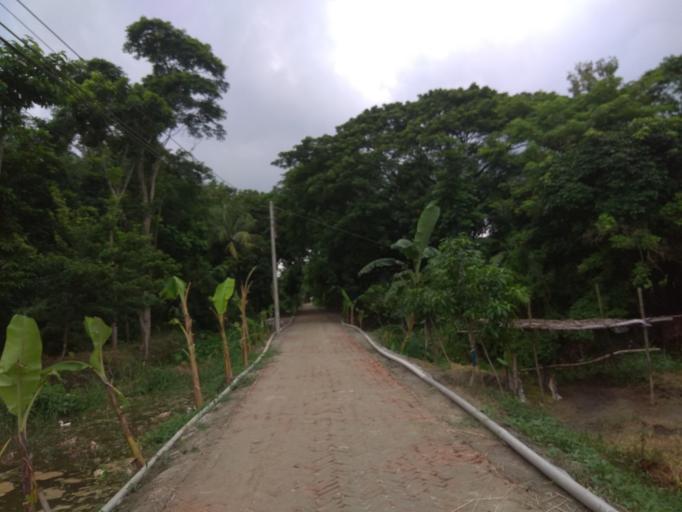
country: BD
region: Dhaka
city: Dohar
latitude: 23.4912
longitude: 90.0382
